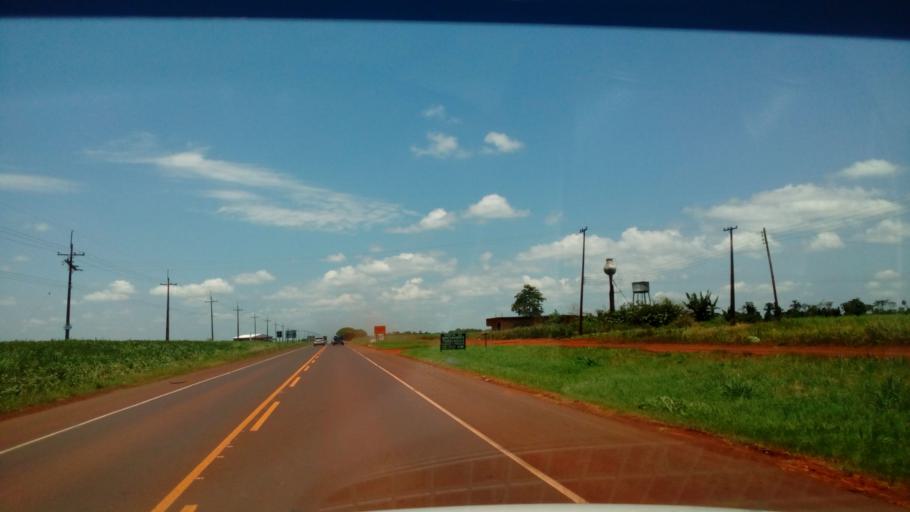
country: PY
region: Alto Parana
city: Naranjal
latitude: -25.9367
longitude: -55.1179
